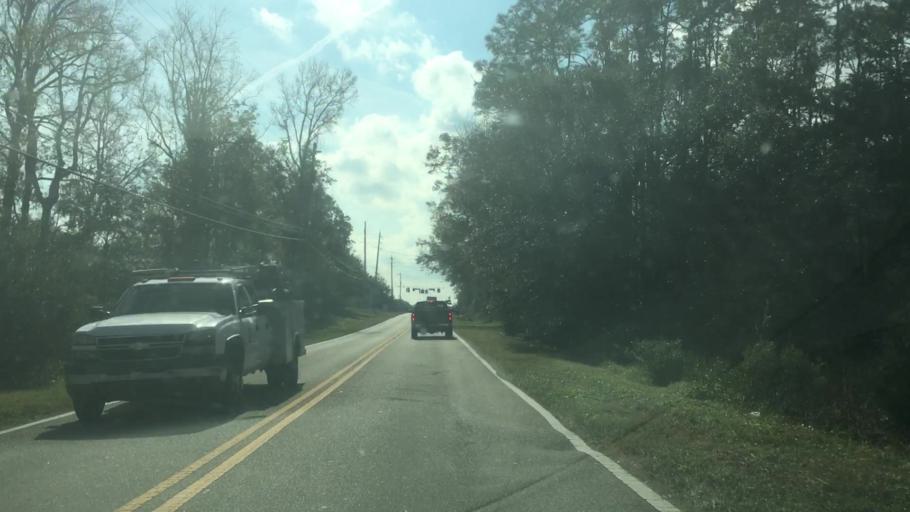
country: US
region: Florida
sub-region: Duval County
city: Jacksonville
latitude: 30.4394
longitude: -81.5796
